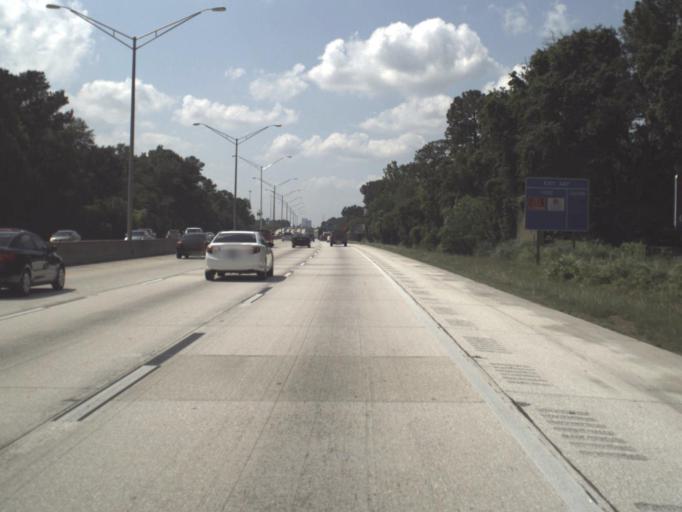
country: US
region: Florida
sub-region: Duval County
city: Jacksonville
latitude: 30.2849
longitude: -81.6235
